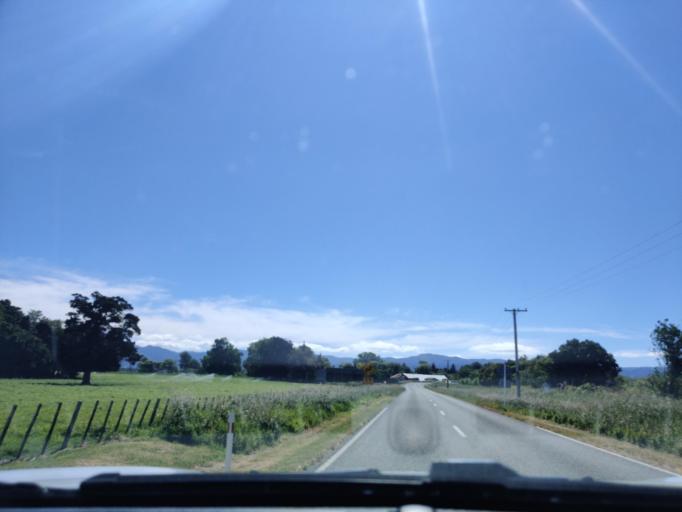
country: NZ
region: Wellington
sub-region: Upper Hutt City
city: Upper Hutt
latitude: -41.2885
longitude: 175.2704
